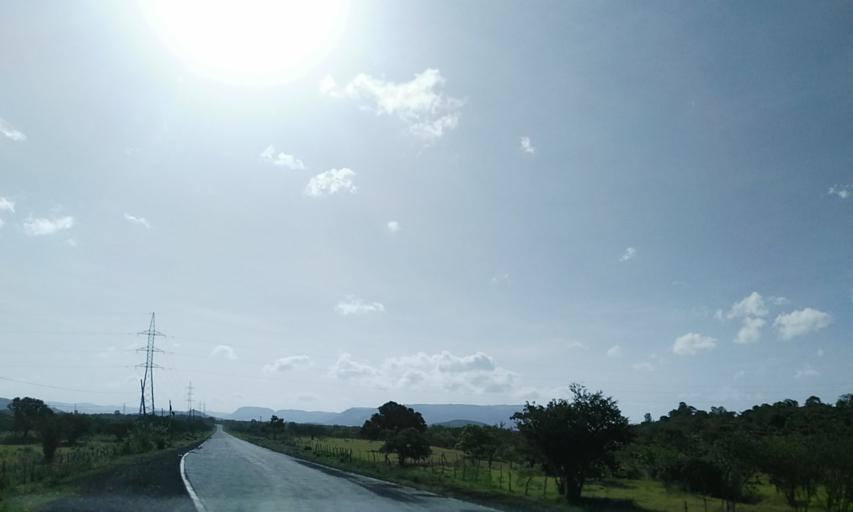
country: NI
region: Matagalpa
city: Ciudad Dario
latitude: 12.7245
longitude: -86.0979
